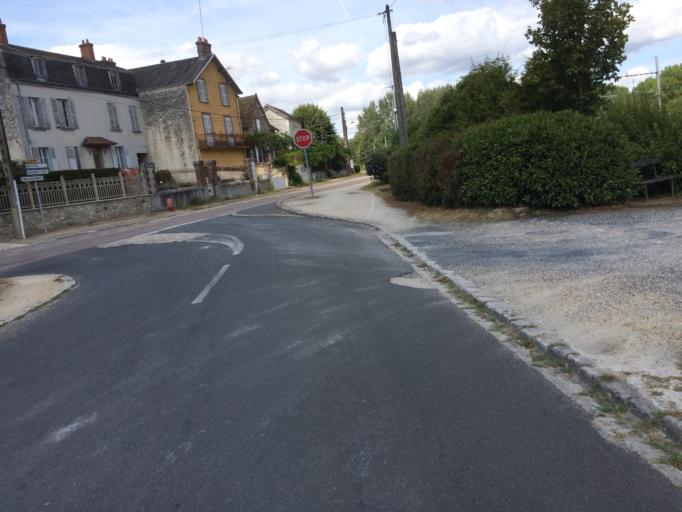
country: FR
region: Ile-de-France
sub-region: Departement de l'Essonne
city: Maisse
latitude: 48.3428
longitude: 2.3787
